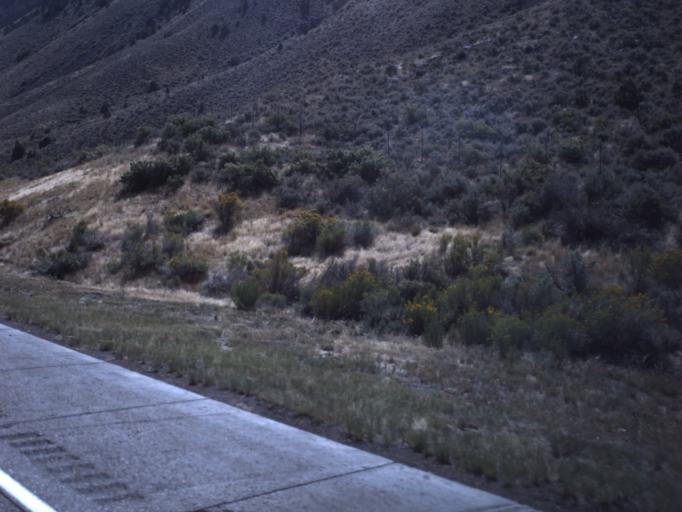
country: US
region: Utah
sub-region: Sevier County
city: Monroe
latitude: 38.5794
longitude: -112.2924
